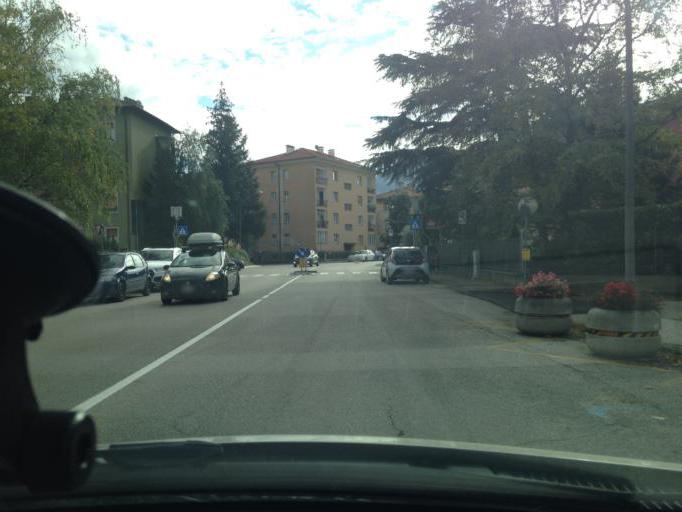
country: IT
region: Trentino-Alto Adige
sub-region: Provincia di Trento
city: Rovereto
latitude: 45.8949
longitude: 11.0376
